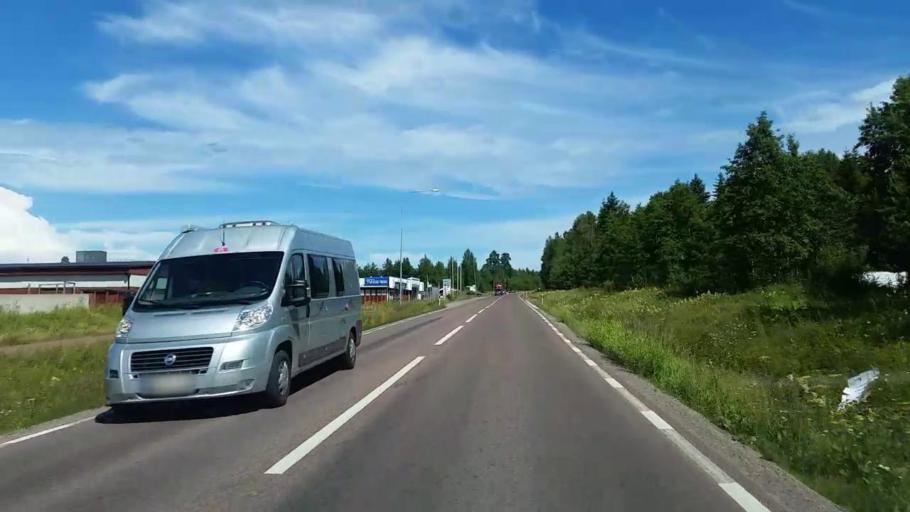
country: SE
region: Dalarna
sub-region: Rattviks Kommun
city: Raettvik
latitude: 60.8940
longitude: 15.1466
